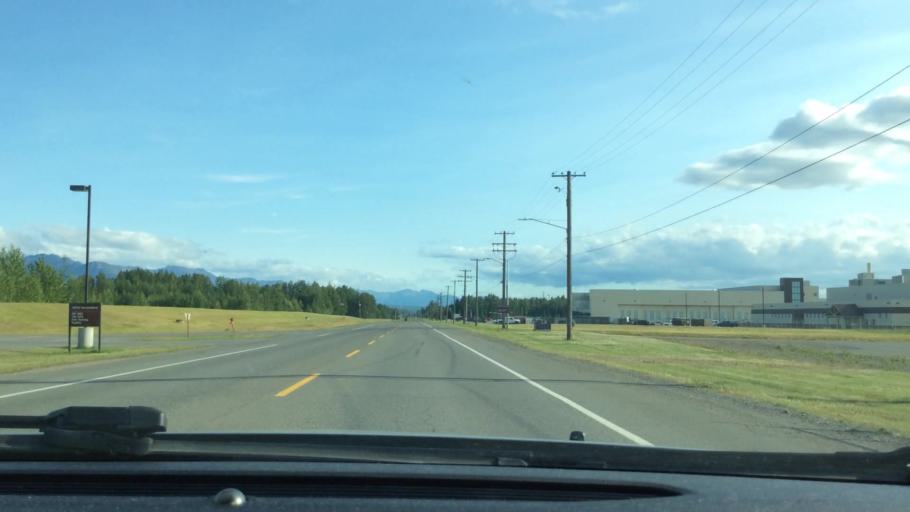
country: US
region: Alaska
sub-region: Anchorage Municipality
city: Anchorage
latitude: 61.2468
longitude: -149.7786
